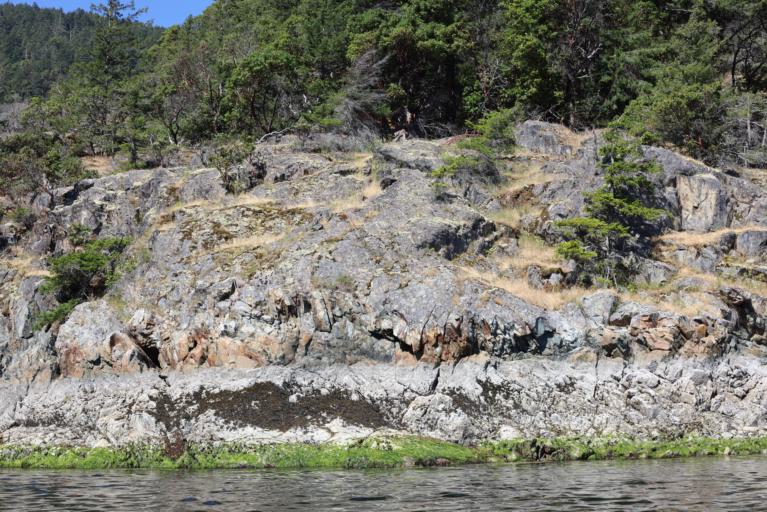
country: CA
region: British Columbia
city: North Cowichan
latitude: 48.8395
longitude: -123.5869
